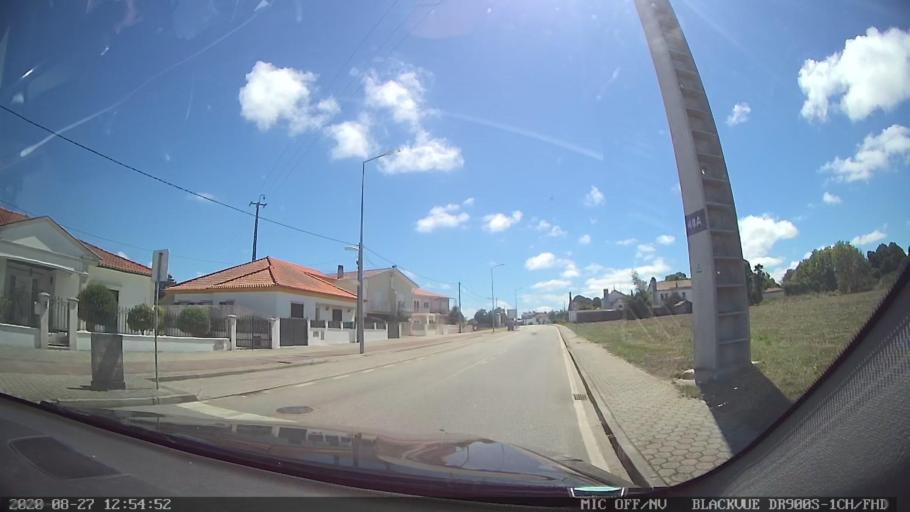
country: PT
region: Aveiro
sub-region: Ilhavo
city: Ilhavo
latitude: 40.5906
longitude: -8.6814
